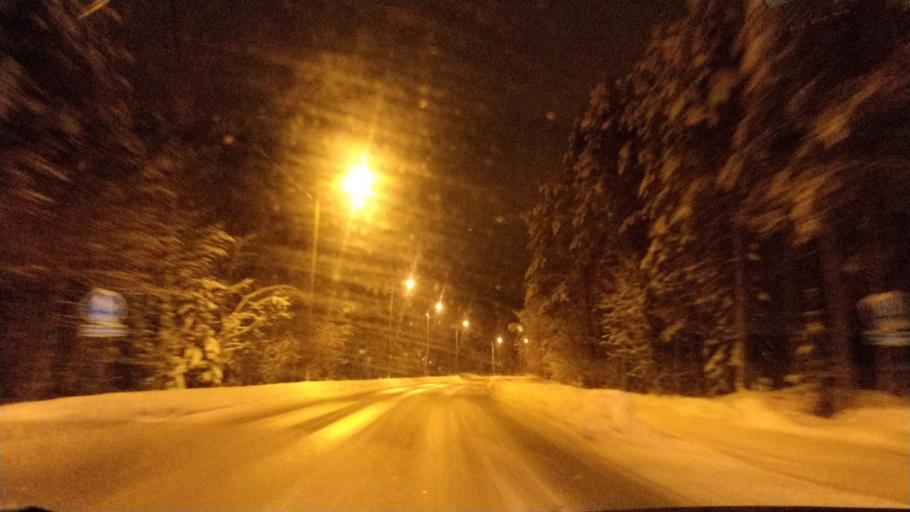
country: FI
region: Lapland
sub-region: Rovaniemi
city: Rovaniemi
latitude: 66.3777
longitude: 25.3820
